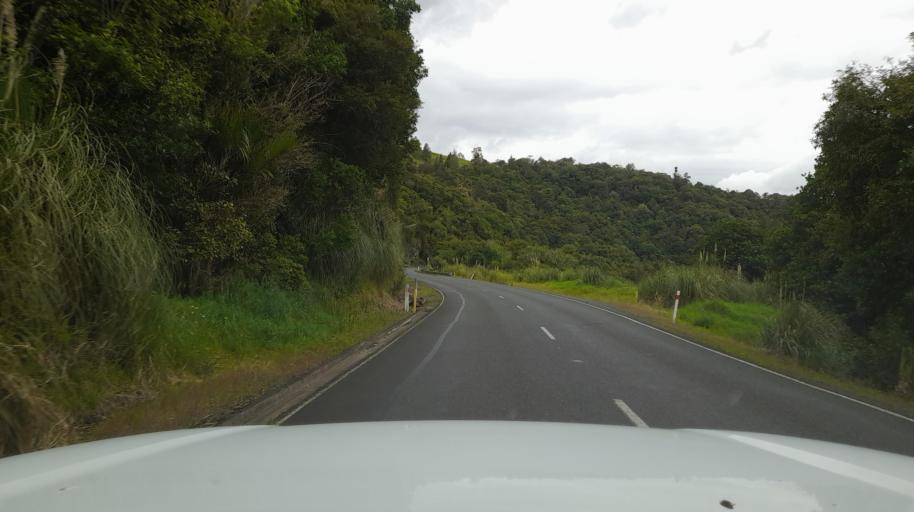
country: NZ
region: Northland
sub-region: Far North District
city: Taipa
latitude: -35.2508
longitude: 173.5319
